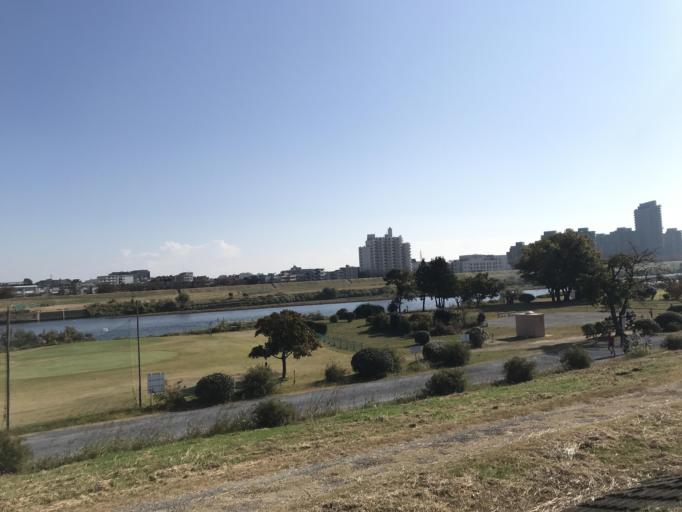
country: JP
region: Kanagawa
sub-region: Kawasaki-shi
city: Kawasaki
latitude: 35.5761
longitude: 139.6701
